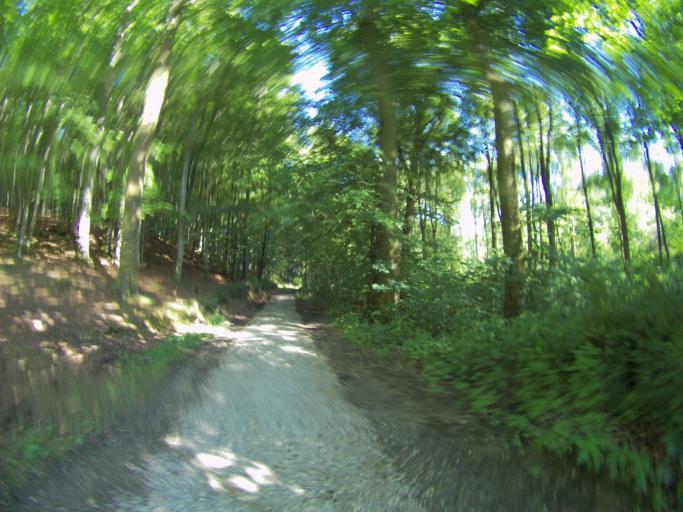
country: DE
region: Bavaria
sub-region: Upper Bavaria
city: Freising
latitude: 48.4149
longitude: 11.7195
